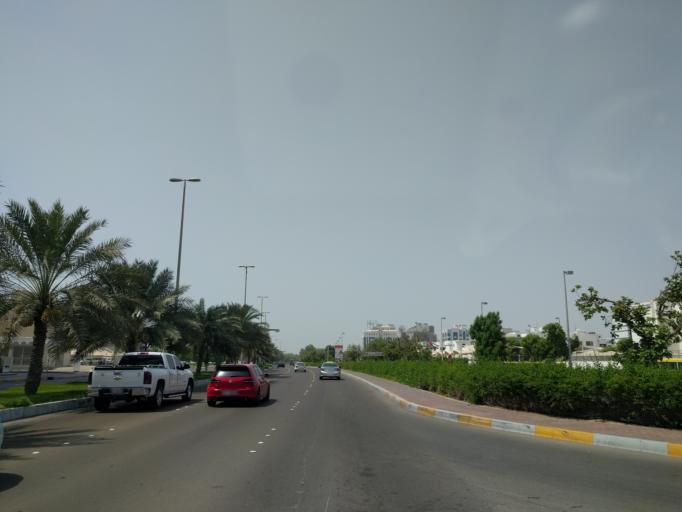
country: AE
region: Abu Dhabi
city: Abu Dhabi
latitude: 24.4295
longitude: 54.4296
